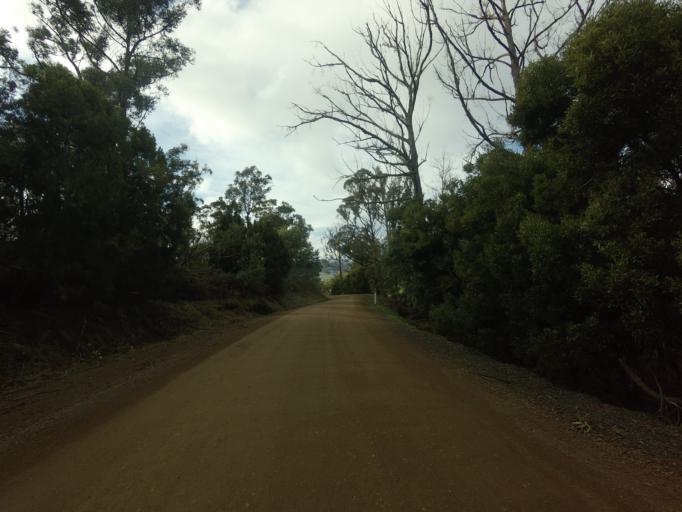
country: AU
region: Tasmania
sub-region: Derwent Valley
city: New Norfolk
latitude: -42.7257
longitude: 146.8688
